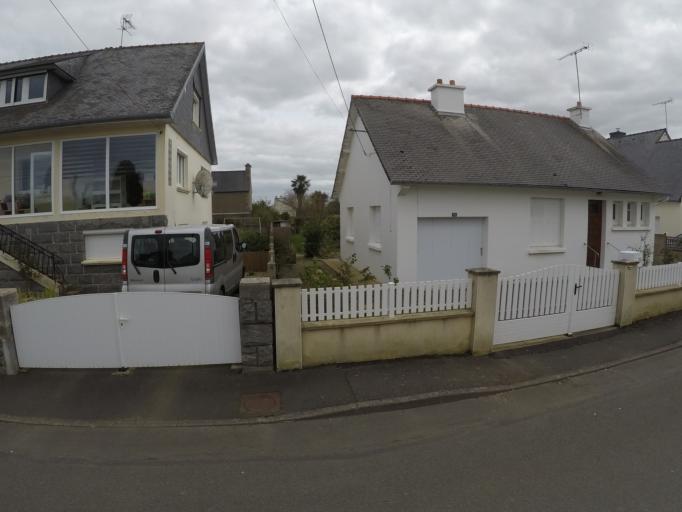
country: FR
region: Brittany
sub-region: Departement des Cotes-d'Armor
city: Plouha
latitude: 48.6792
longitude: -2.9266
